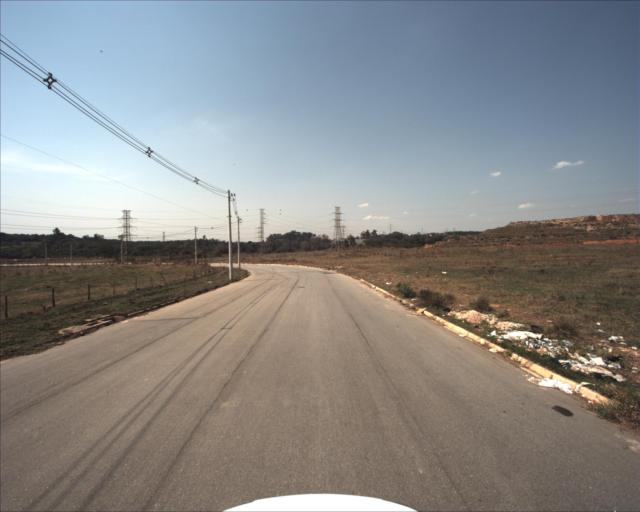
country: BR
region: Sao Paulo
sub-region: Sorocaba
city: Sorocaba
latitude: -23.4227
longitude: -47.4440
